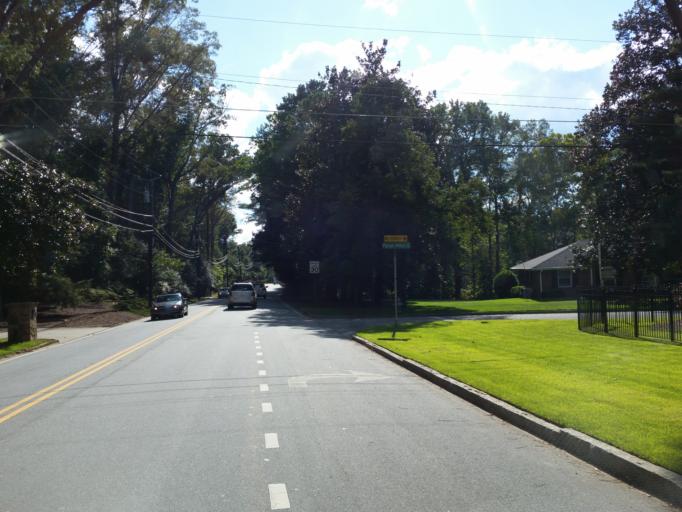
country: US
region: Georgia
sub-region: Cobb County
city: Vinings
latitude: 33.8677
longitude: -84.4355
